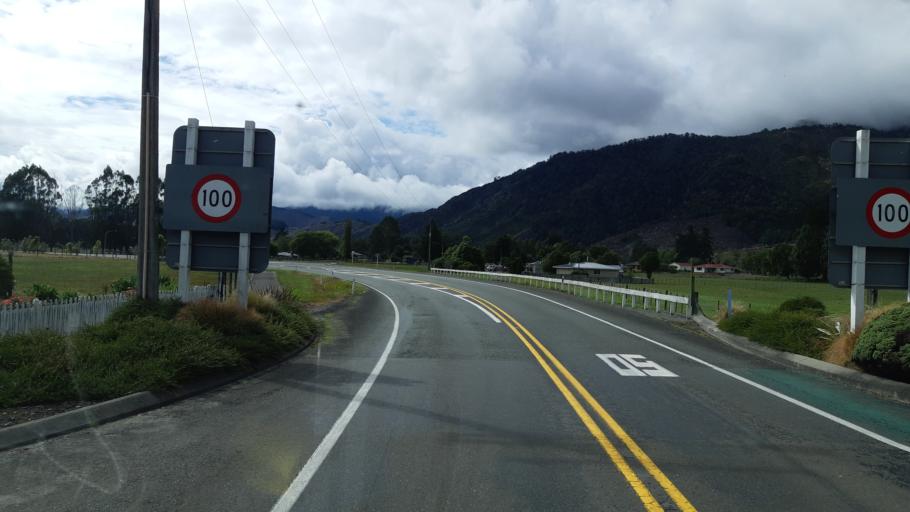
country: NZ
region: West Coast
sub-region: Buller District
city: Westport
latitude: -41.8001
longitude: 172.3339
